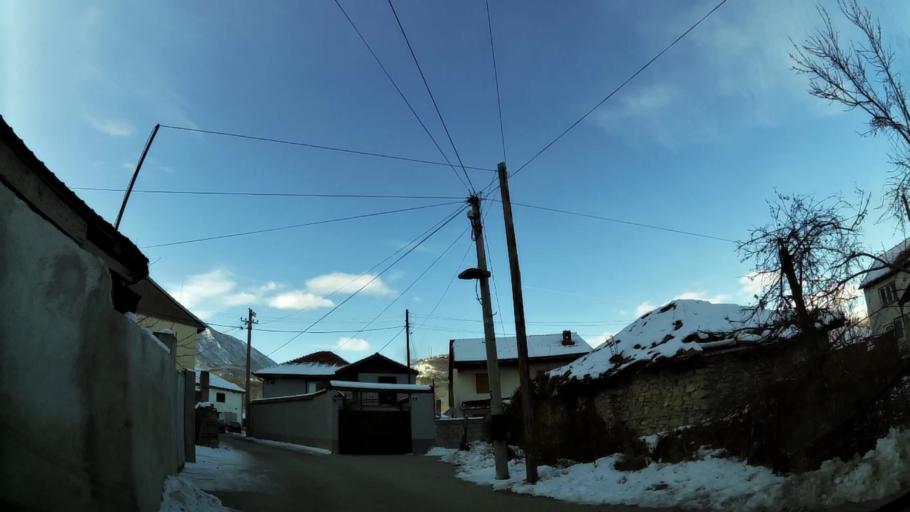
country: MK
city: Grchec
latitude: 41.9739
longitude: 21.3100
